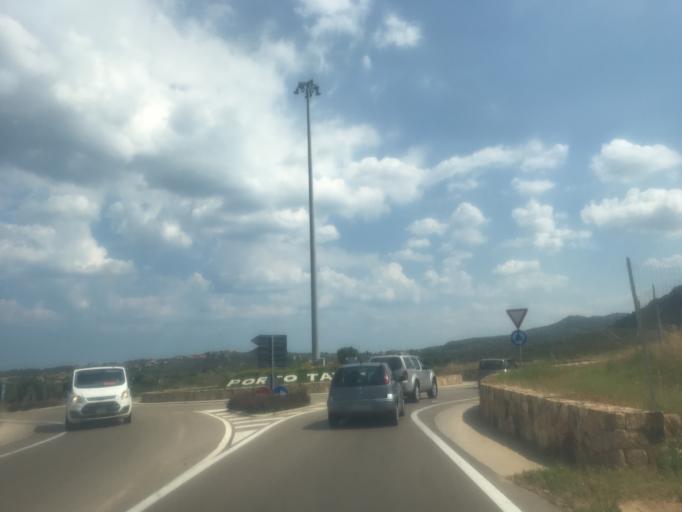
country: IT
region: Sardinia
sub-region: Provincia di Olbia-Tempio
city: San Teodoro
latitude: 40.8574
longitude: 9.6434
